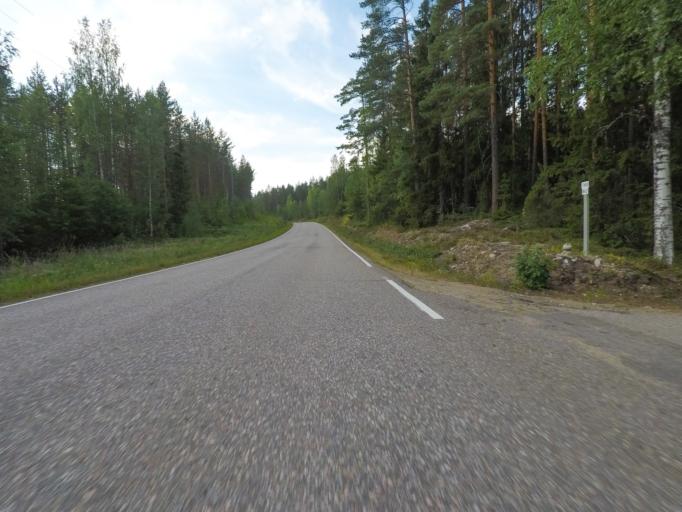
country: FI
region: Southern Savonia
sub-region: Savonlinna
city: Sulkava
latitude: 61.7352
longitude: 28.2067
